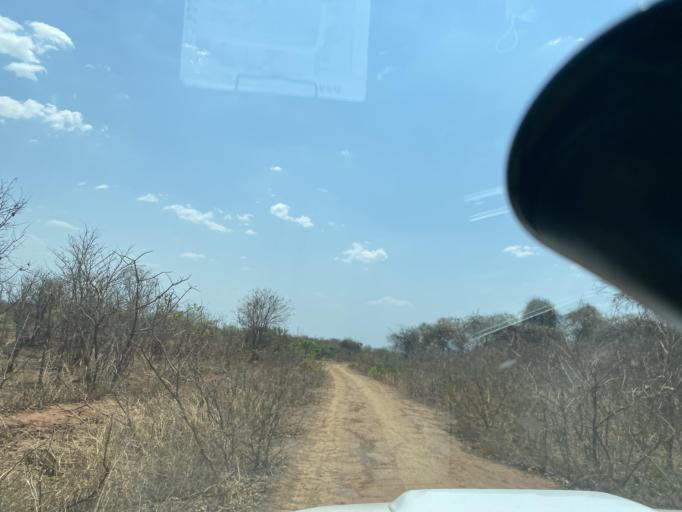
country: ZM
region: Lusaka
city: Lusaka
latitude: -15.5055
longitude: 27.9713
